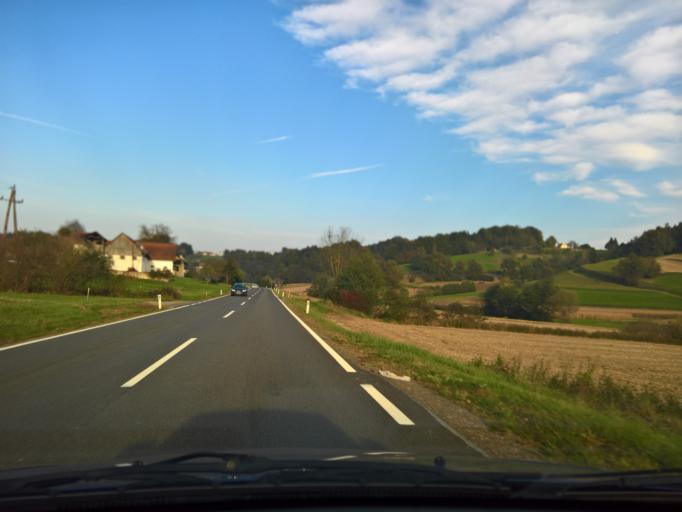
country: AT
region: Styria
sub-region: Politischer Bezirk Leibnitz
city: Grossklein
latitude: 46.7368
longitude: 15.4588
